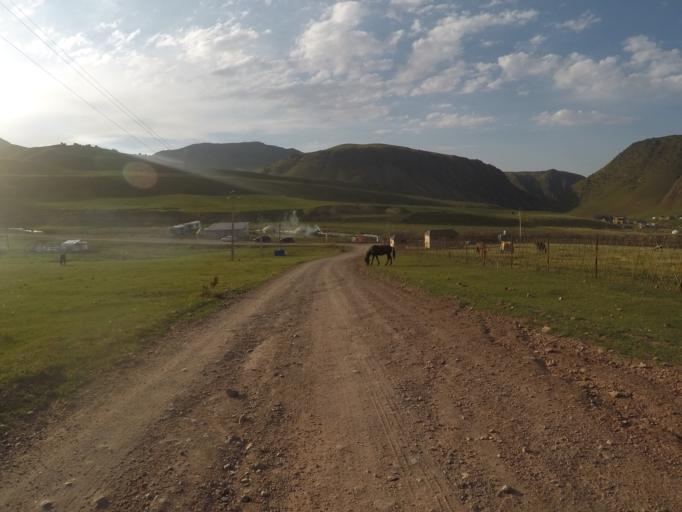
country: KG
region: Chuy
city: Bishkek
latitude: 42.6339
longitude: 74.6161
